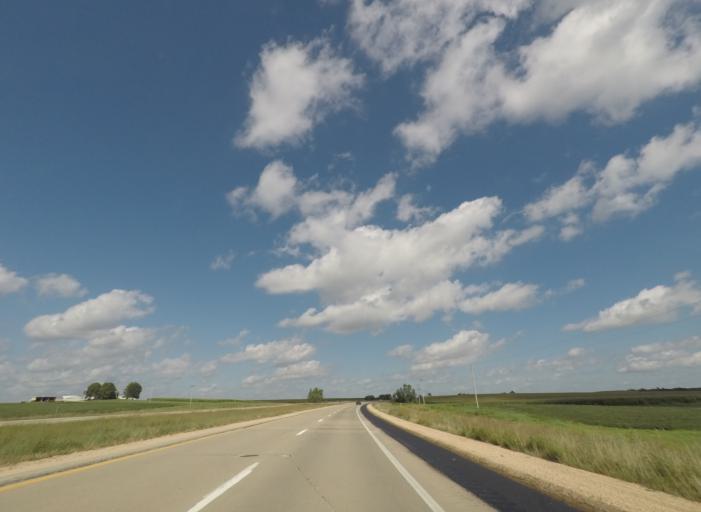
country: US
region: Iowa
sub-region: Jones County
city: Monticello
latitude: 42.2796
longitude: -91.1326
